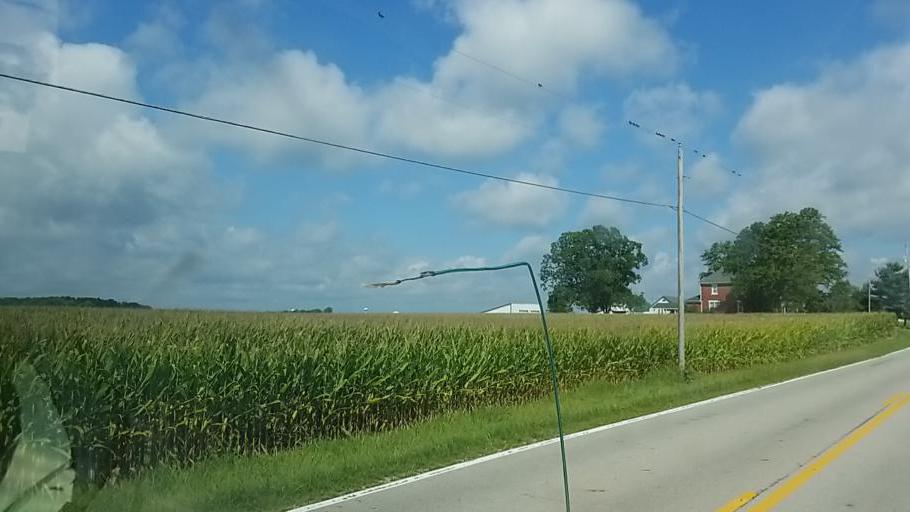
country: US
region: Ohio
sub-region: Pickaway County
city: Commercial Point
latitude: 39.7891
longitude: -83.1222
